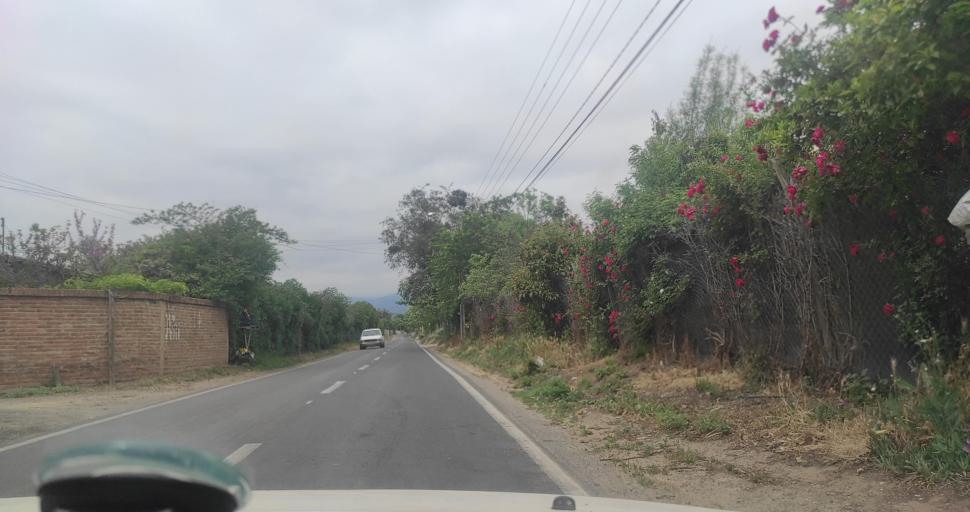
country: CL
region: Valparaiso
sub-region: Provincia de Marga Marga
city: Limache
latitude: -33.0168
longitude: -71.2366
